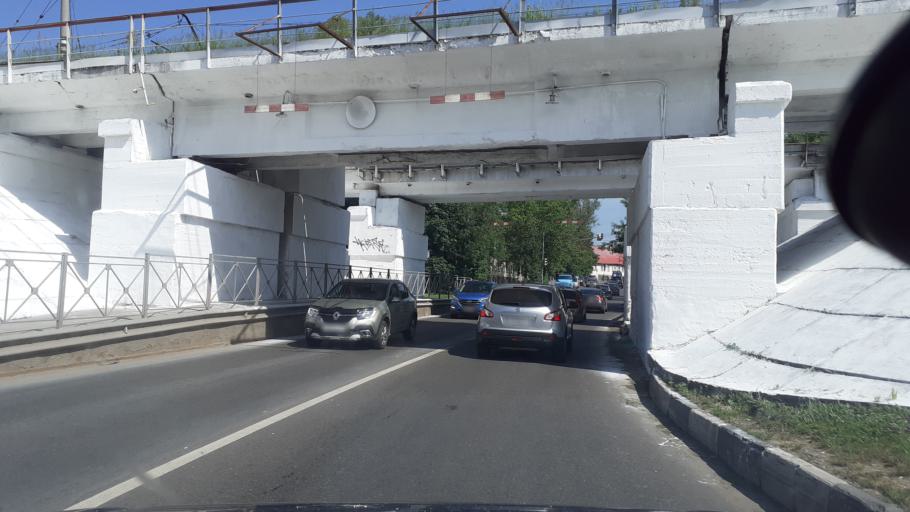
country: RU
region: Moskovskaya
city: Naro-Fominsk
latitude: 55.3835
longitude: 36.7381
